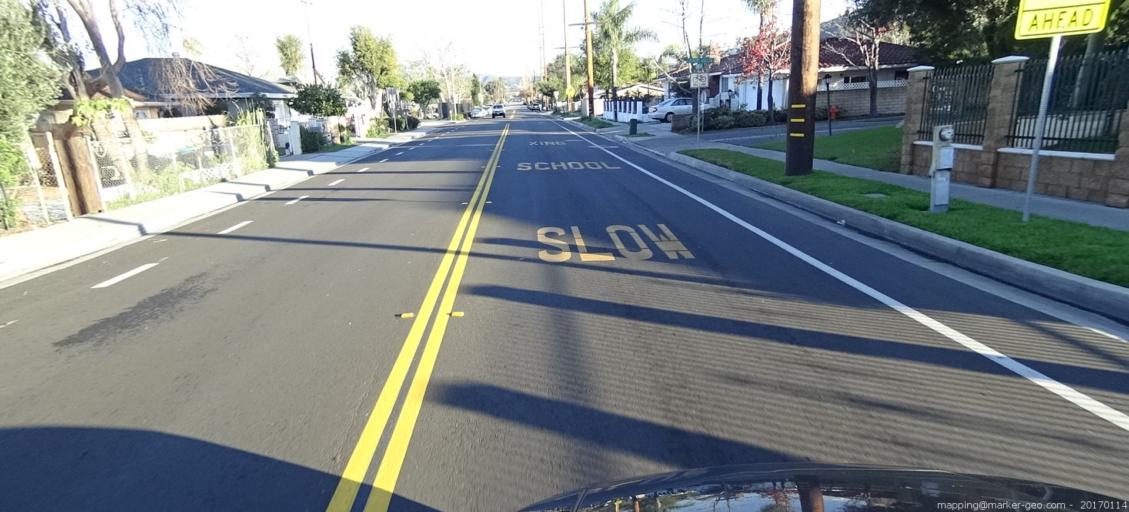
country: US
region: California
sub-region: Orange County
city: Villa Park
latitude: 33.7906
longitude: -117.8013
